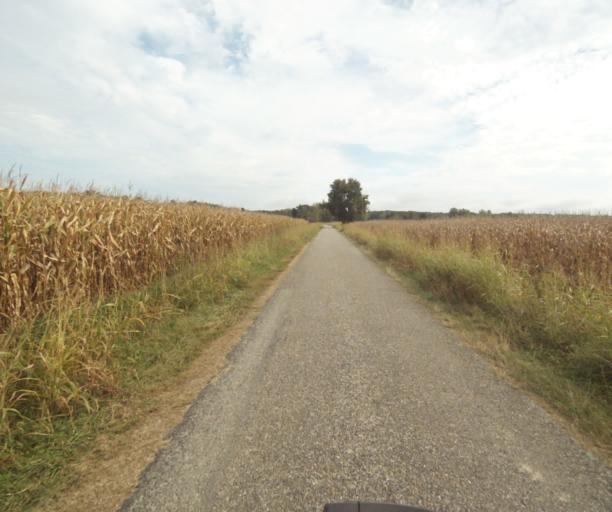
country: FR
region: Midi-Pyrenees
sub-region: Departement du Tarn-et-Garonne
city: Finhan
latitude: 43.9093
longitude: 1.2501
